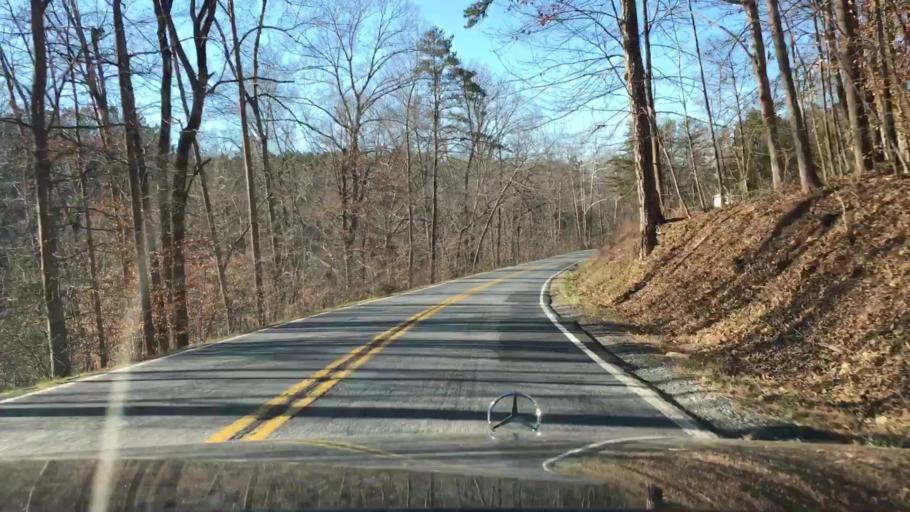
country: US
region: Virginia
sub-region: Pittsylvania County
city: Motley
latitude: 37.1529
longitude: -79.3744
